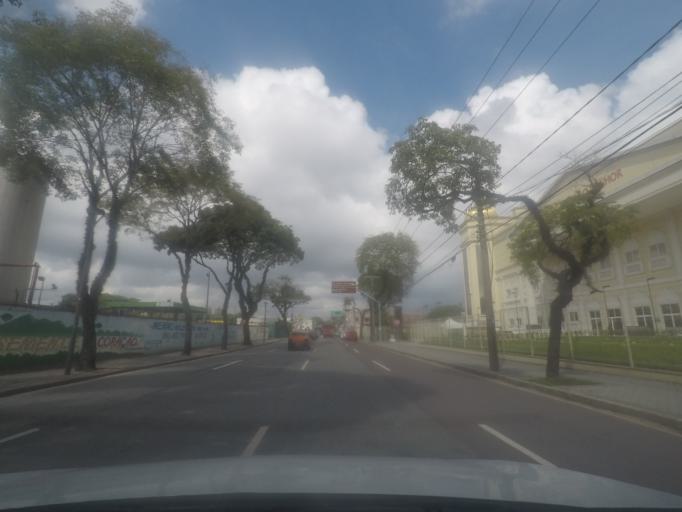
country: BR
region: Parana
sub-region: Curitiba
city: Curitiba
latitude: -25.4413
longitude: -49.2612
